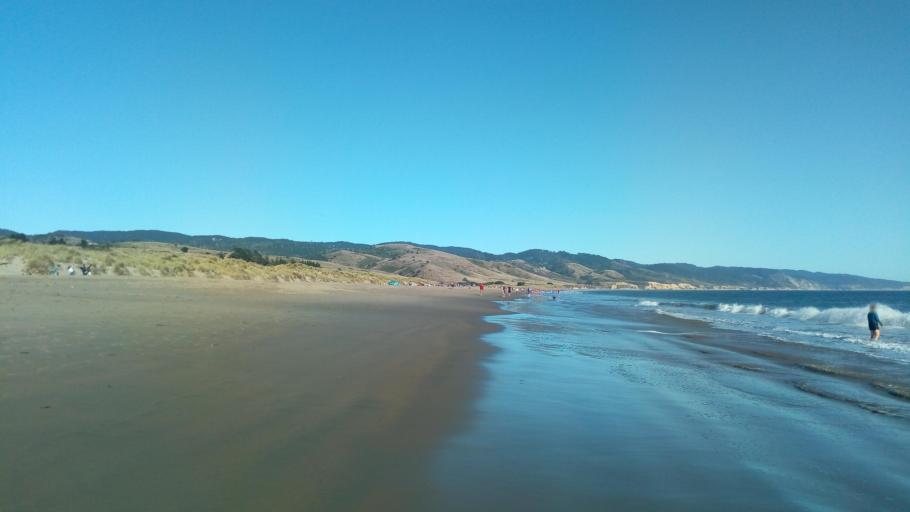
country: US
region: California
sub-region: Marin County
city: Inverness
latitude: 38.0258
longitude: -122.8870
